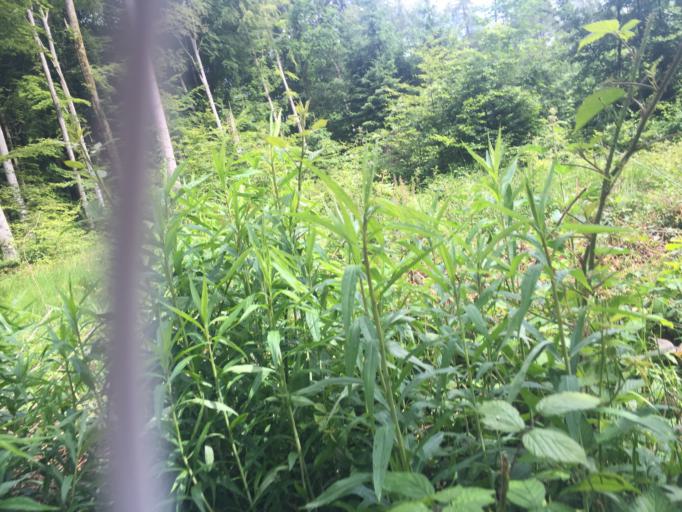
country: CH
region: Bern
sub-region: Bern-Mittelland District
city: Koniz
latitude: 46.9365
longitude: 7.4104
